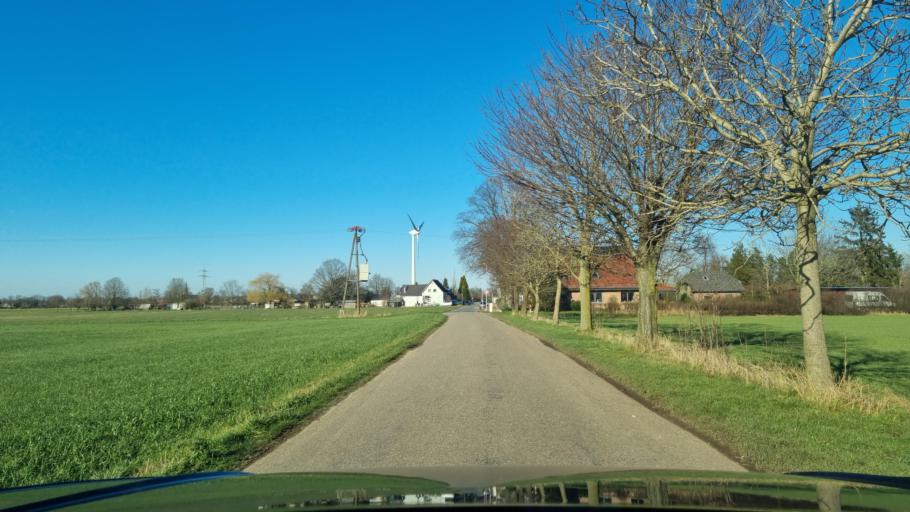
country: DE
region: North Rhine-Westphalia
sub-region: Regierungsbezirk Dusseldorf
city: Kleve
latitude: 51.8101
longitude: 6.1706
